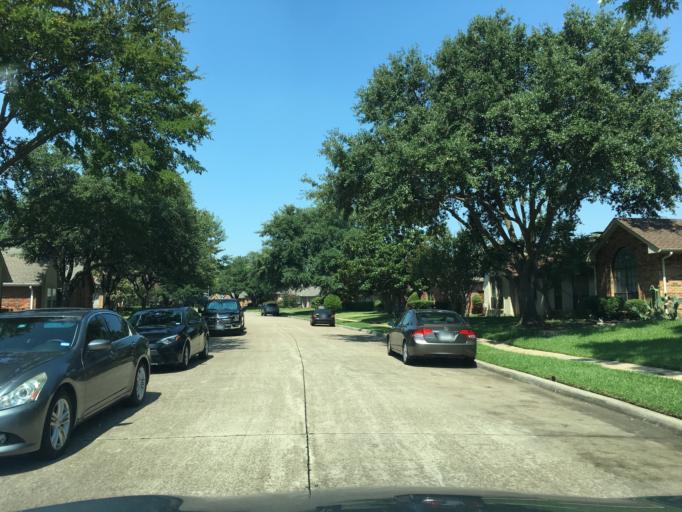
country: US
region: Texas
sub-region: Dallas County
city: Garland
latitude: 32.9405
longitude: -96.6697
